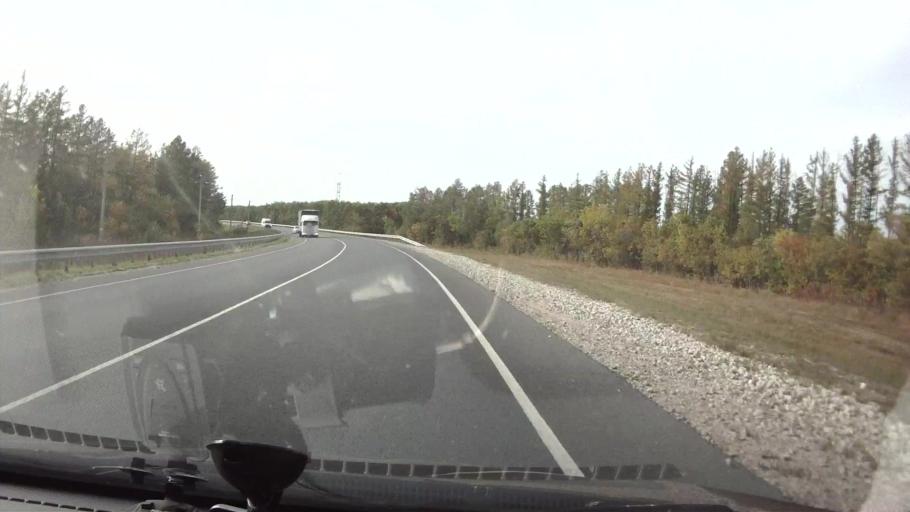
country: RU
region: Saratov
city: Shikhany
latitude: 52.1614
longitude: 47.1679
